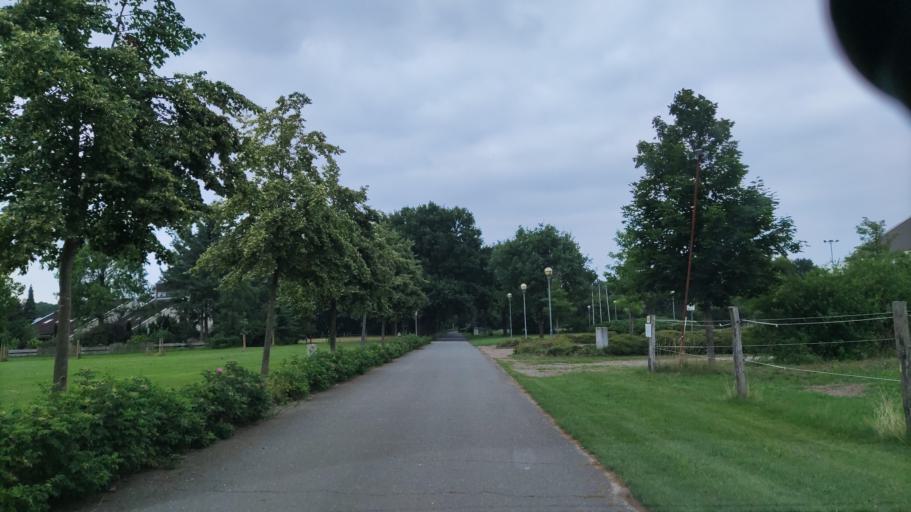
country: DE
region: Lower Saxony
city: Bad Fallingbostel
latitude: 52.8023
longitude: 9.6516
